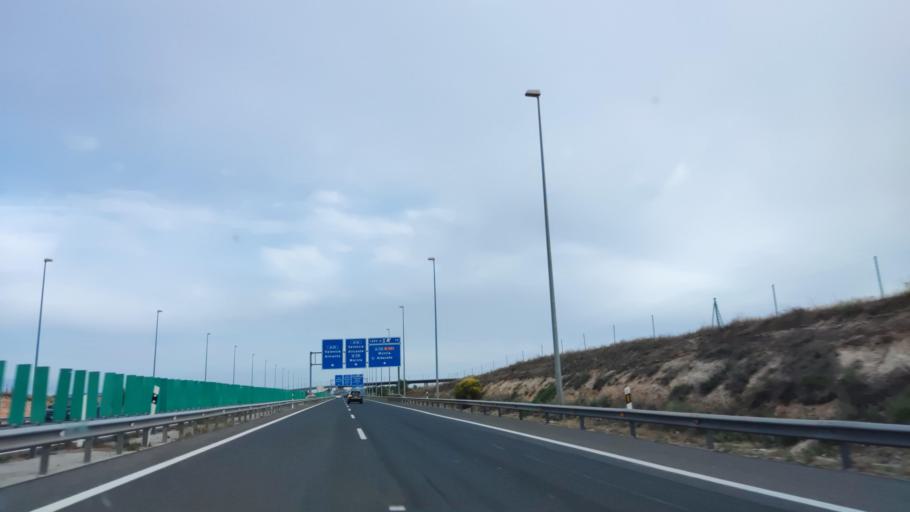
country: ES
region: Castille-La Mancha
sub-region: Provincia de Albacete
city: Albacete
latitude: 38.9824
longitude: -1.8244
